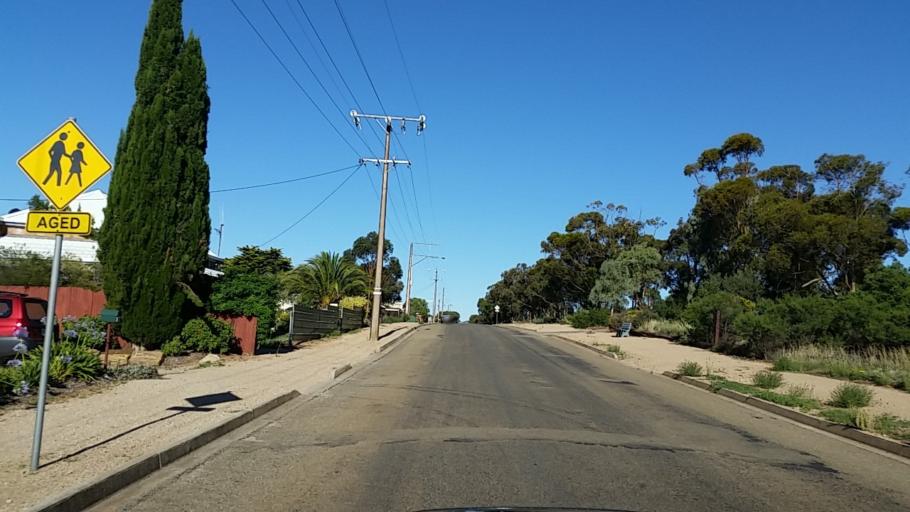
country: AU
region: South Australia
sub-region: Peterborough
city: Peterborough
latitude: -32.9798
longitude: 138.8284
